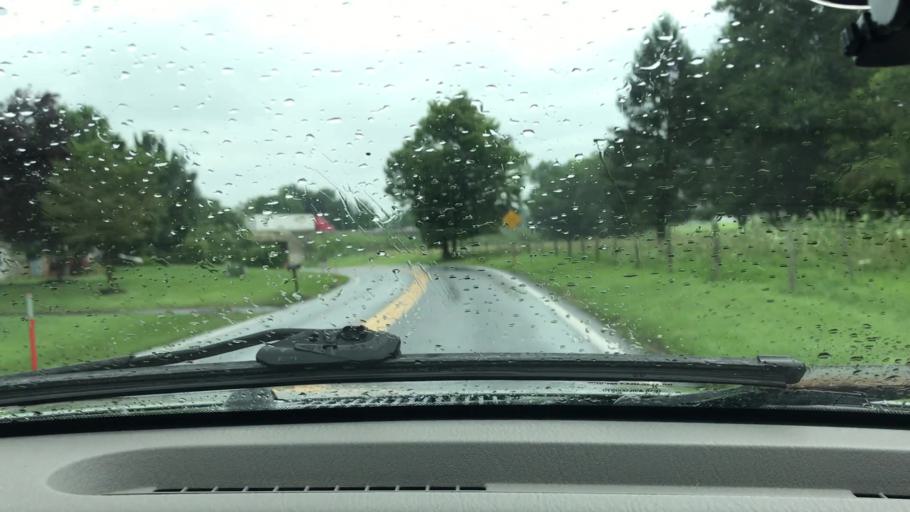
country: US
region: Pennsylvania
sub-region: Lancaster County
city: Elizabethtown
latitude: 40.2065
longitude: -76.6341
